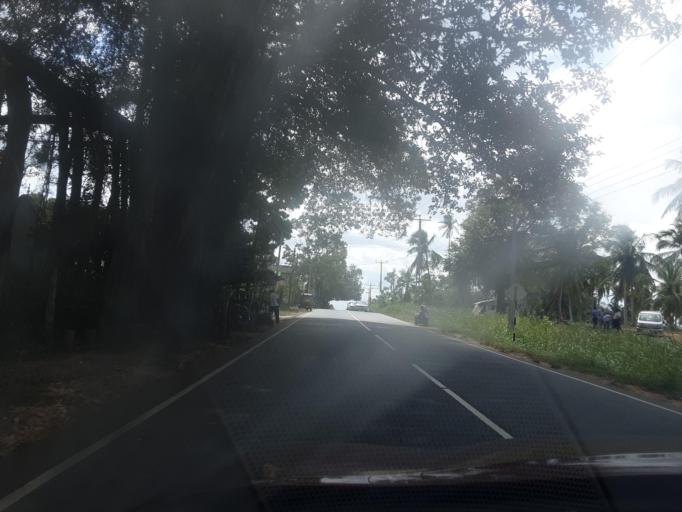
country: LK
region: North Western
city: Kuliyapitiya
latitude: 7.4827
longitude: 79.9851
